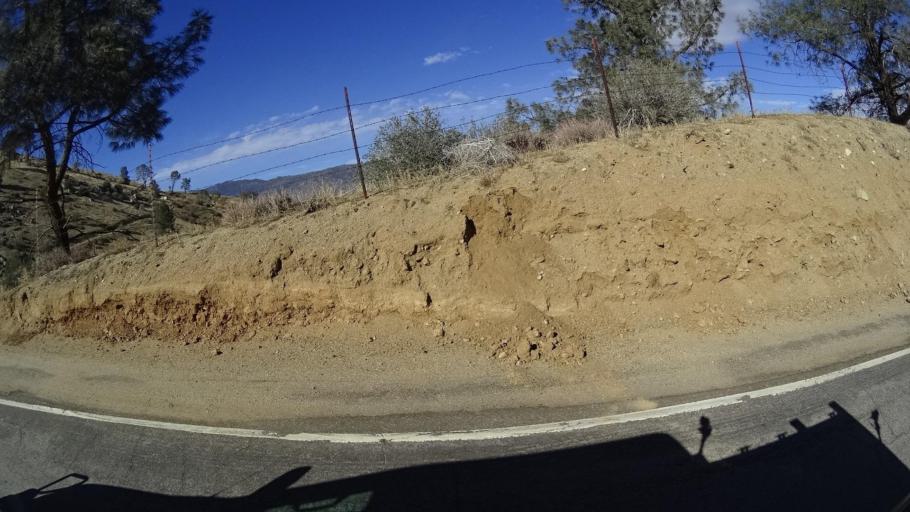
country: US
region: California
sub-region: Kern County
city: Bodfish
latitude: 35.5807
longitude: -118.5048
